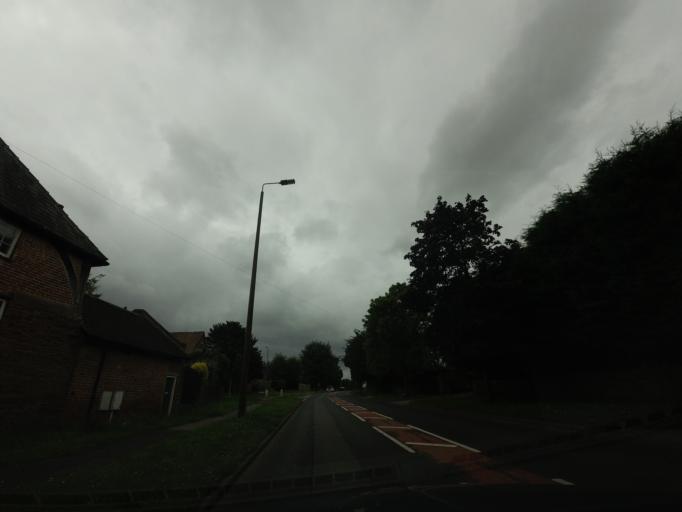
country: GB
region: England
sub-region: Nottinghamshire
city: Kimberley
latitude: 53.0080
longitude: -1.2542
